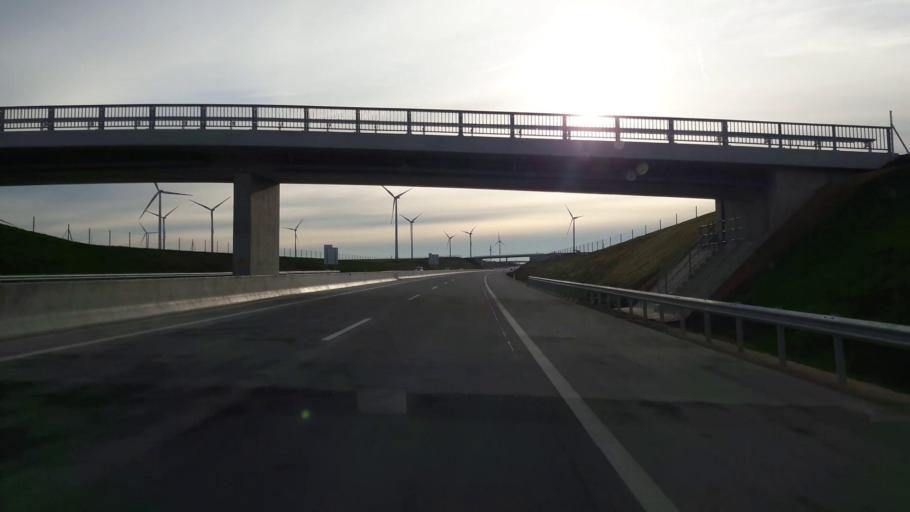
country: AT
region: Lower Austria
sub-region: Politischer Bezirk Mistelbach
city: Grosskrut
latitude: 48.6440
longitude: 16.6875
